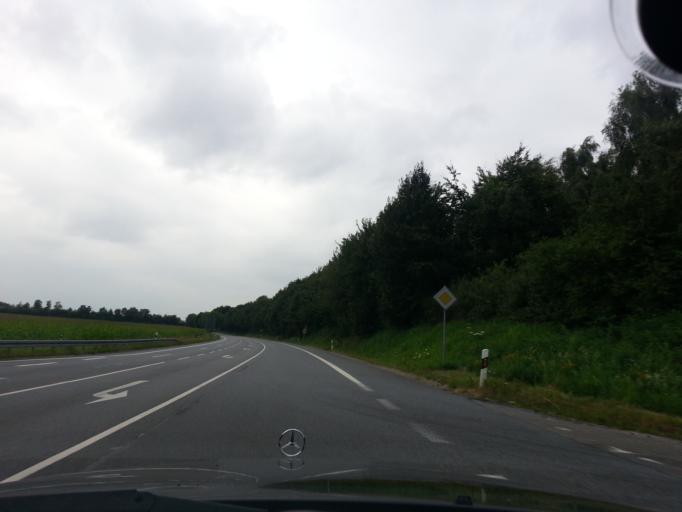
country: DE
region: North Rhine-Westphalia
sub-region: Regierungsbezirk Munster
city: Borken
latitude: 51.8303
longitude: 6.8488
